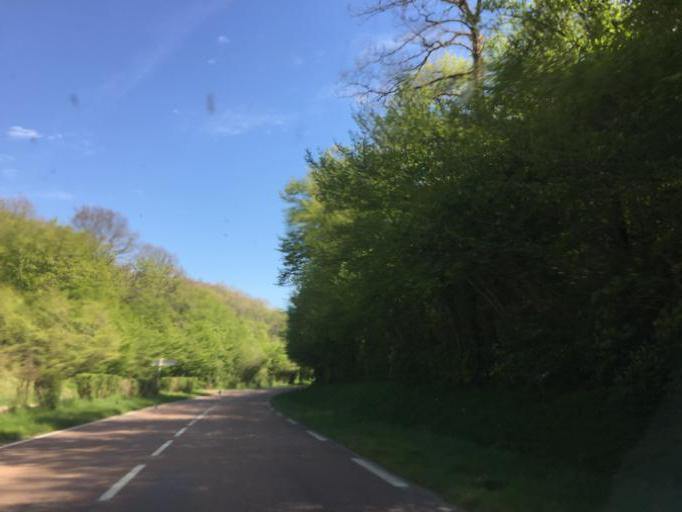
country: FR
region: Bourgogne
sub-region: Departement de la Nievre
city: Clamecy
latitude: 47.4510
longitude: 3.6376
